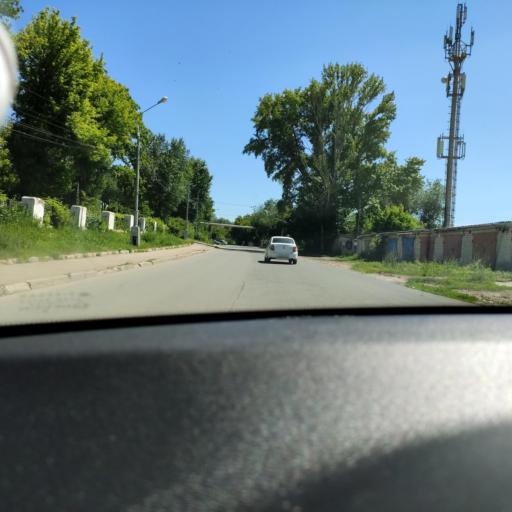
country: RU
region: Samara
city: Volzhskiy
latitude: 53.3823
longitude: 50.1727
